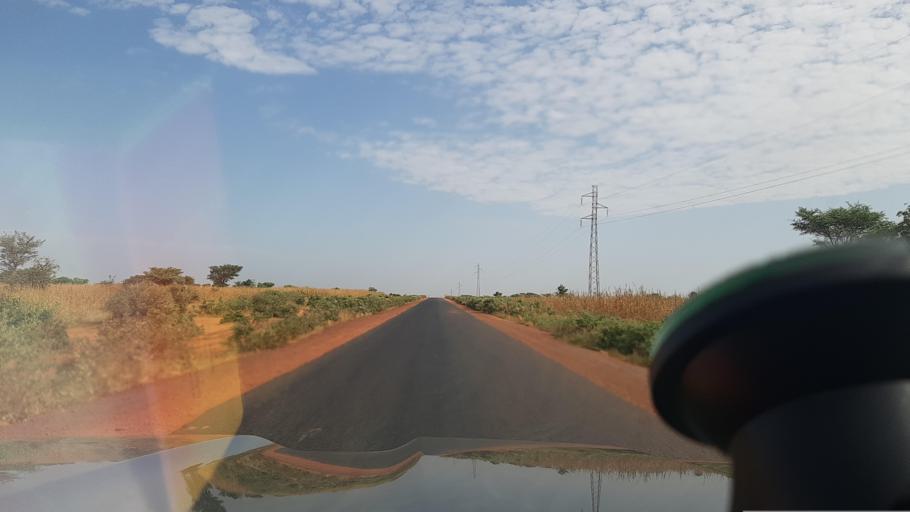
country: ML
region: Segou
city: Segou
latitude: 13.5417
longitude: -6.1213
